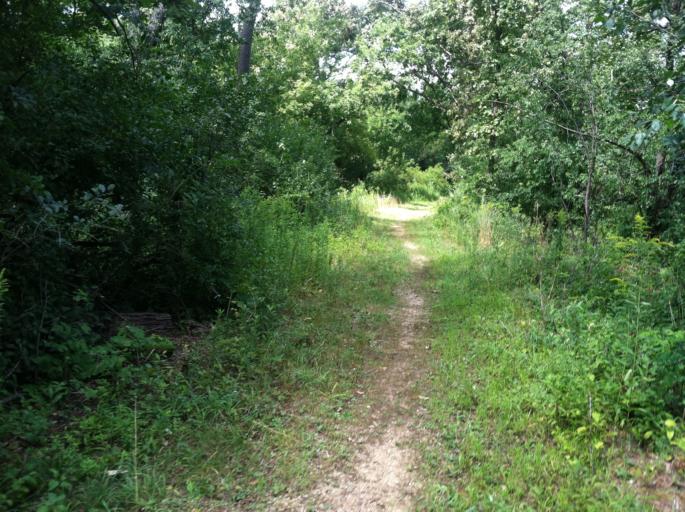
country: US
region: Illinois
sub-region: Cook County
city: Wheeling
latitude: 42.1500
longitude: -87.9104
